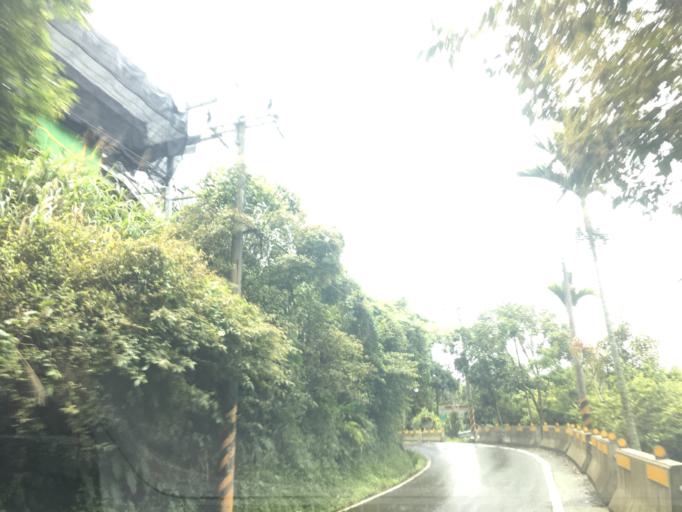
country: TW
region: Taiwan
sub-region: Yunlin
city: Douliu
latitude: 23.5531
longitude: 120.6729
